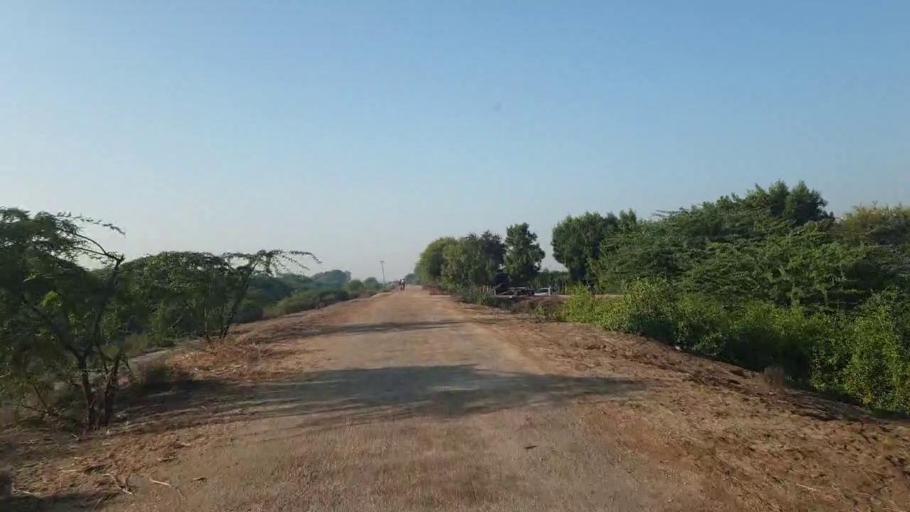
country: PK
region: Sindh
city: Badin
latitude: 24.5988
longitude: 68.7747
